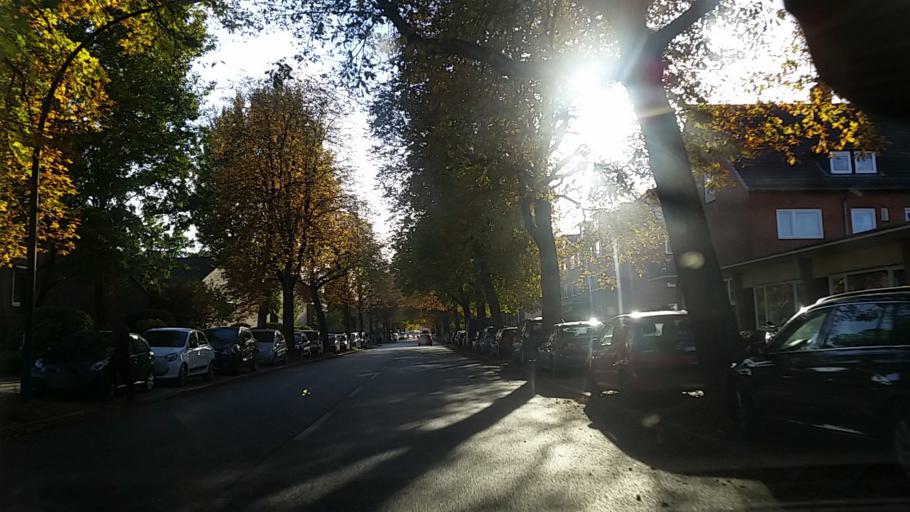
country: DE
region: Hamburg
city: Farmsen-Berne
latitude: 53.5914
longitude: 10.1352
